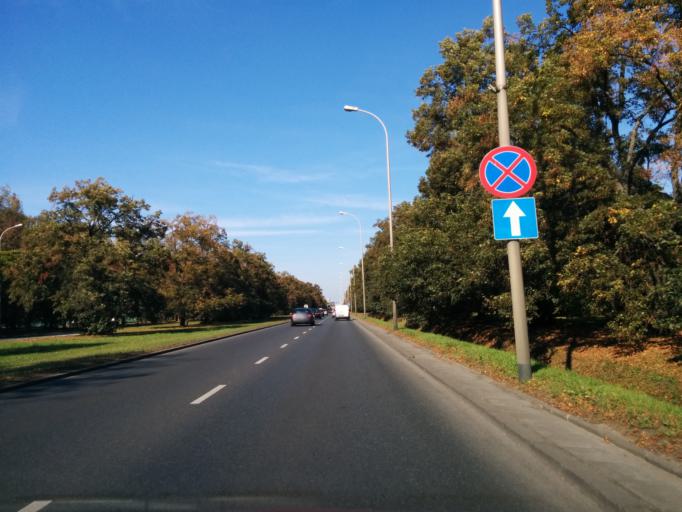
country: PL
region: Masovian Voivodeship
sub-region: Warszawa
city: Wlochy
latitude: 52.1851
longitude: 20.9795
